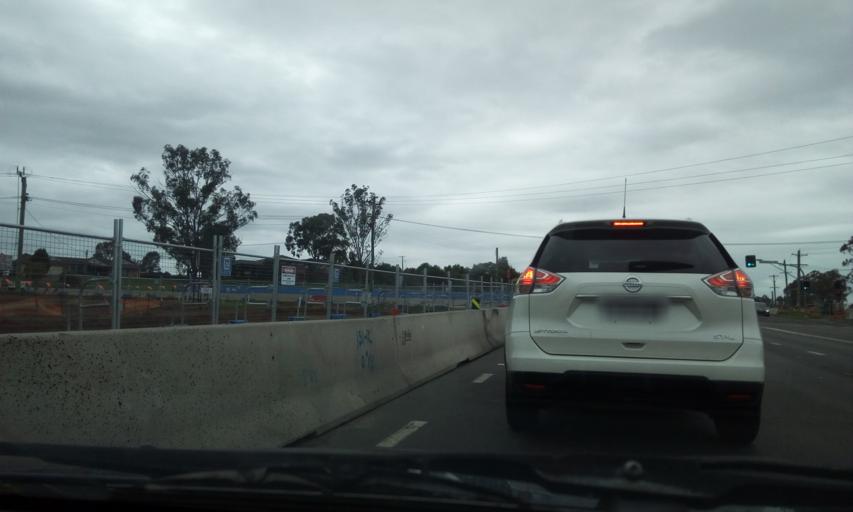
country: AU
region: New South Wales
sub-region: Penrith Municipality
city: Kingswood Park
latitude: -33.7751
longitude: 150.7120
